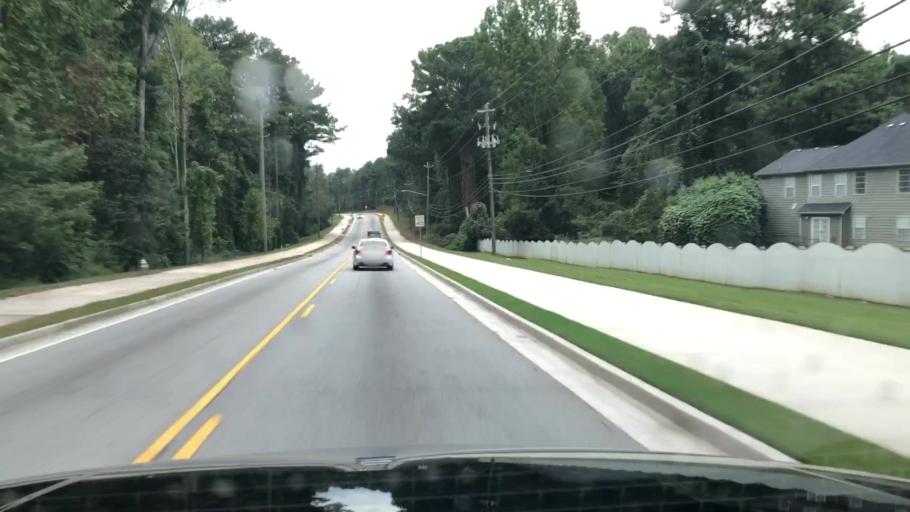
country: US
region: Georgia
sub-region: Cobb County
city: Mableton
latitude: 33.7066
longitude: -84.5538
